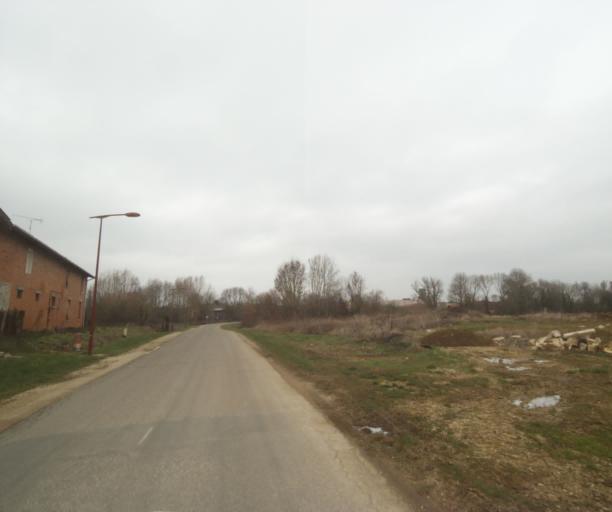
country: FR
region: Champagne-Ardenne
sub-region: Departement de la Marne
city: Pargny-sur-Saulx
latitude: 48.6918
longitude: 4.8046
